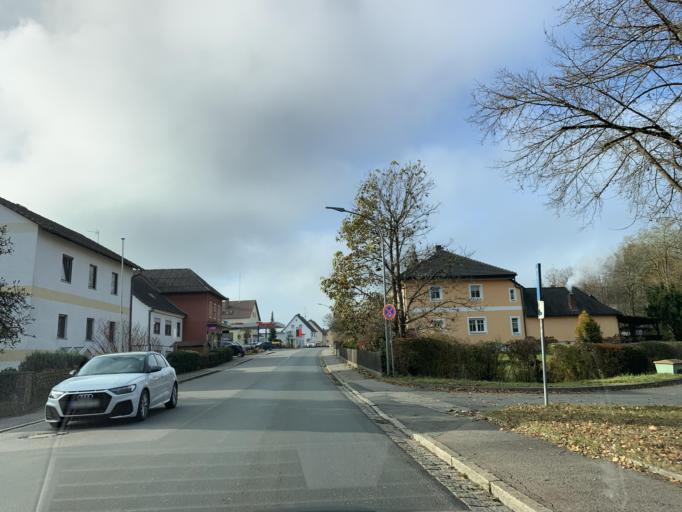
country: DE
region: Bavaria
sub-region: Upper Palatinate
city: Bodenwohr
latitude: 49.2688
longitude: 12.3023
